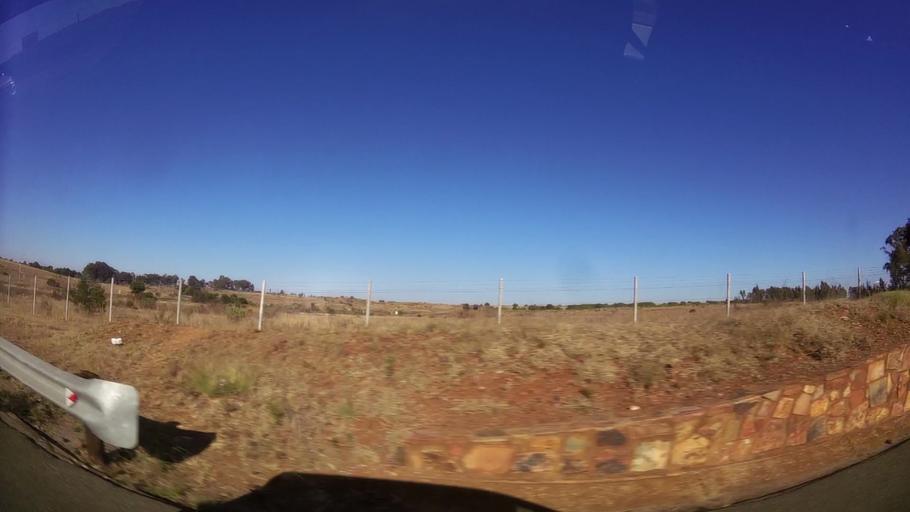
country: ZA
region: Gauteng
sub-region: City of Tshwane Metropolitan Municipality
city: Centurion
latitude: -25.8185
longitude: 28.2375
